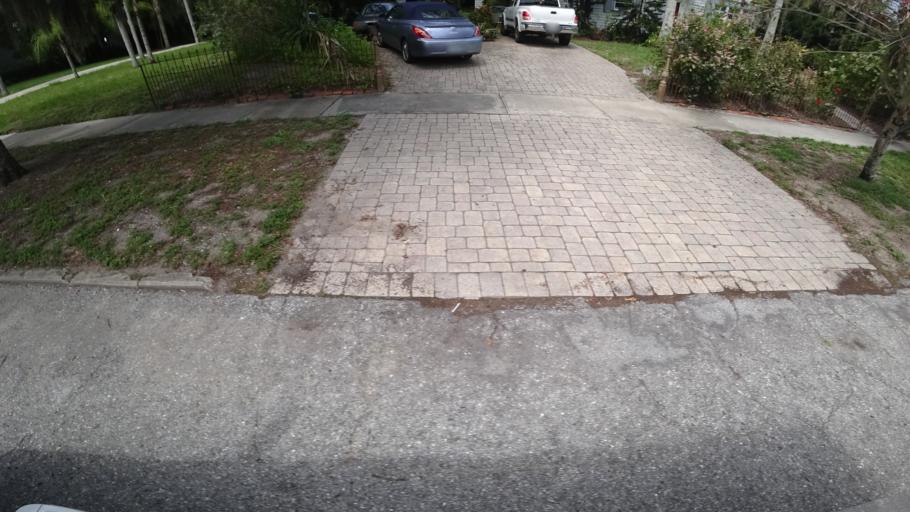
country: US
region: Florida
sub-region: Manatee County
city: Whitfield
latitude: 27.4049
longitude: -82.5718
